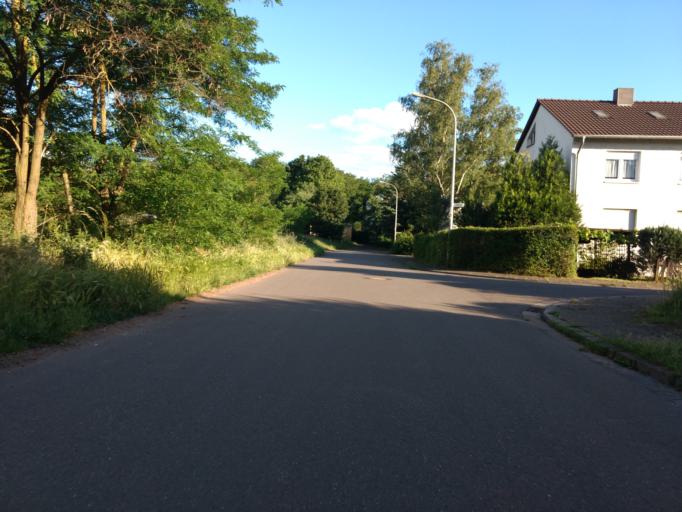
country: DE
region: Saarland
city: Dillingen
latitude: 49.3410
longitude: 6.7441
